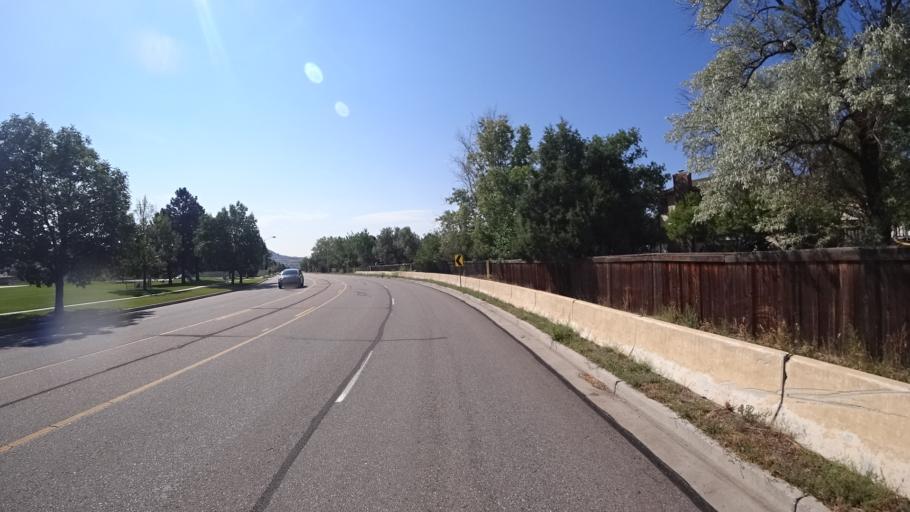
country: US
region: Colorado
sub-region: El Paso County
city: Air Force Academy
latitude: 38.9215
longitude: -104.8276
